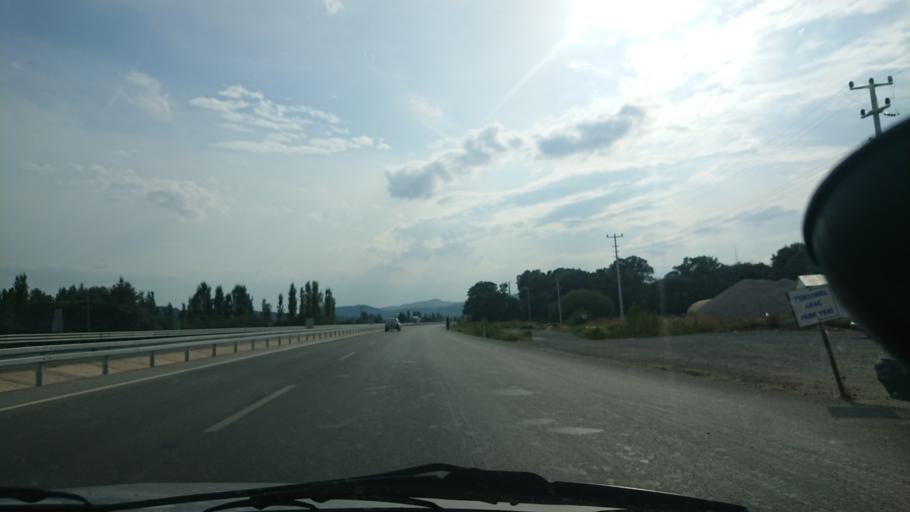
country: TR
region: Kuetahya
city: Gediz
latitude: 38.9445
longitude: 29.3285
